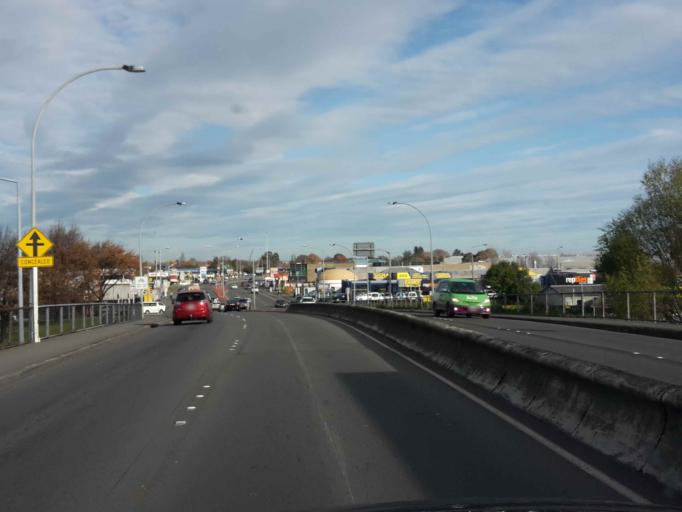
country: NZ
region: Canterbury
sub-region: Selwyn District
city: Prebbleton
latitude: -43.5411
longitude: 172.5499
